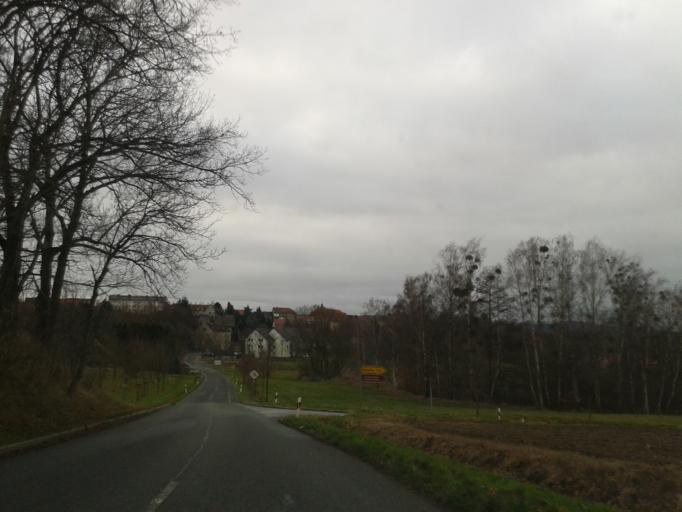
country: DE
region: Saxony
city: Weissenberg
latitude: 51.2013
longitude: 14.6632
